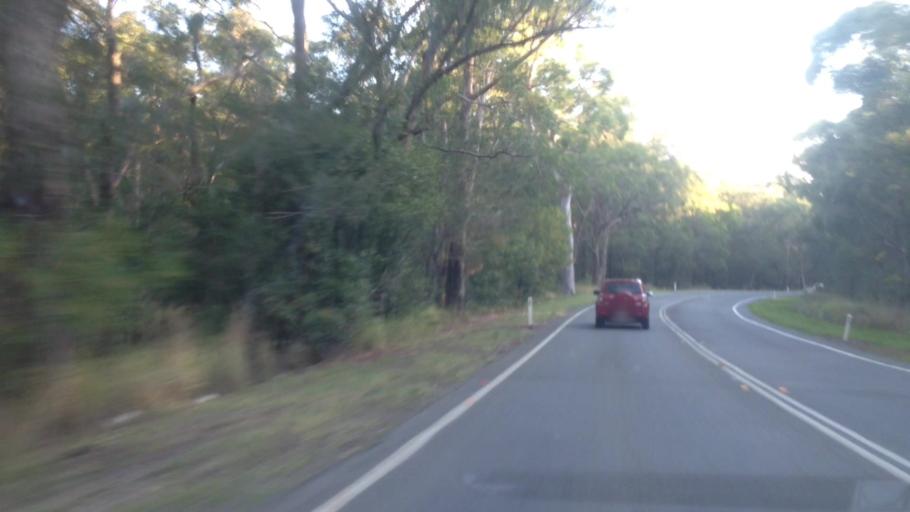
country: AU
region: New South Wales
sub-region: Lake Macquarie Shire
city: Dora Creek
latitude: -33.0000
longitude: 151.4921
